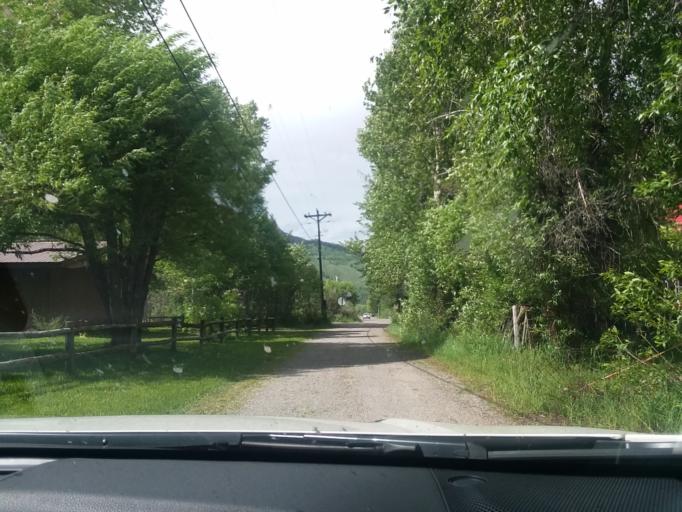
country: US
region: Wyoming
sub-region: Teton County
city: Wilson
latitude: 43.4995
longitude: -110.8720
